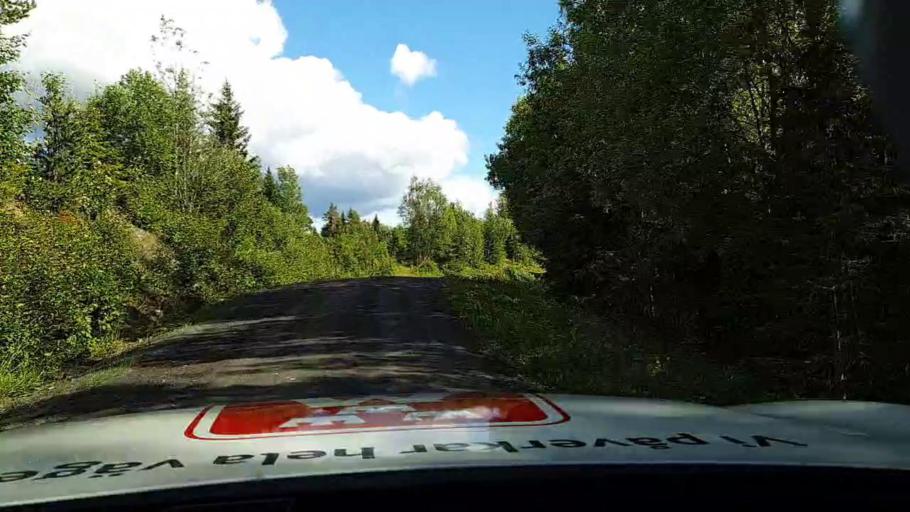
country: SE
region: Jaemtland
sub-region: Krokoms Kommun
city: Valla
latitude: 63.3210
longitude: 13.7583
